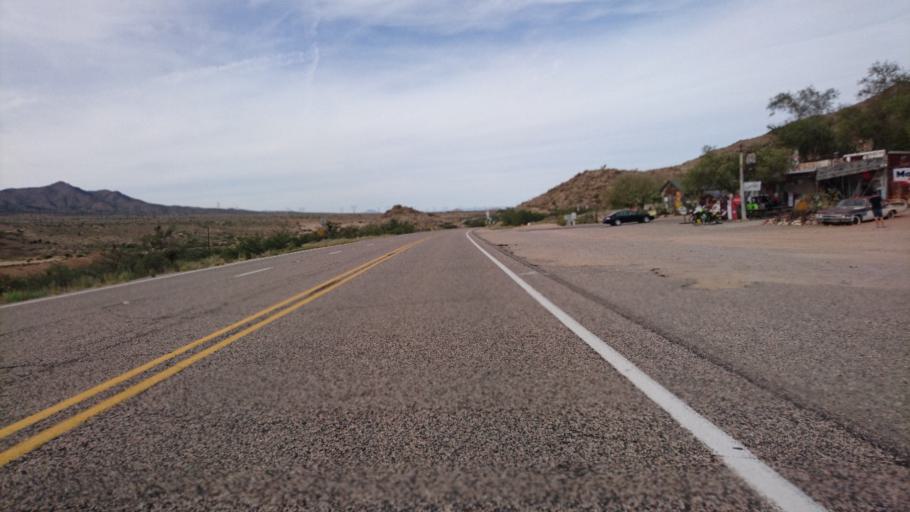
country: US
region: Arizona
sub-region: Mohave County
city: New Kingman-Butler
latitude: 35.3745
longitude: -113.7226
